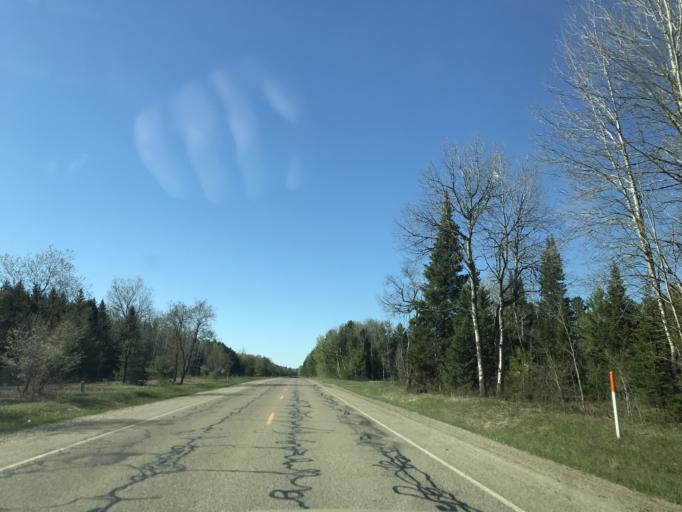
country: US
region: Michigan
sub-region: Crawford County
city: Grayling
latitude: 44.7477
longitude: -84.7515
